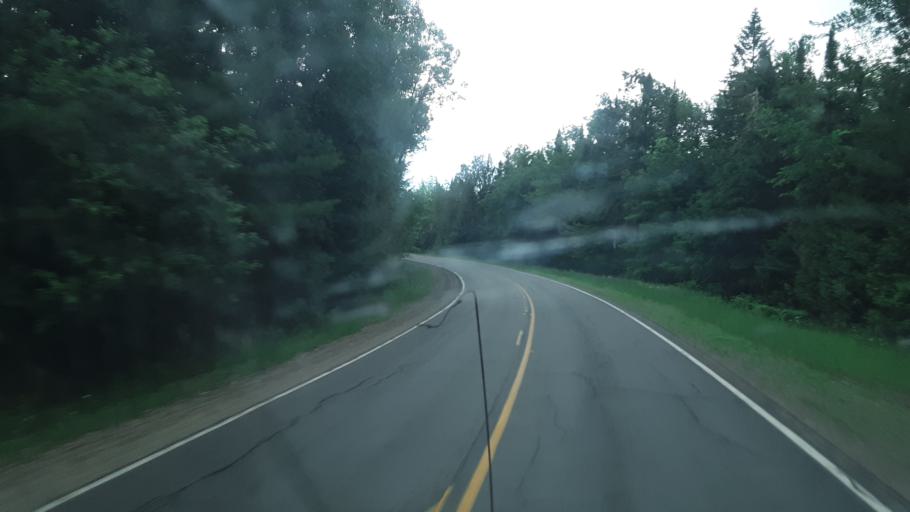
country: US
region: Maine
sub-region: Penobscot County
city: Medway
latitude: 45.7045
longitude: -68.2932
